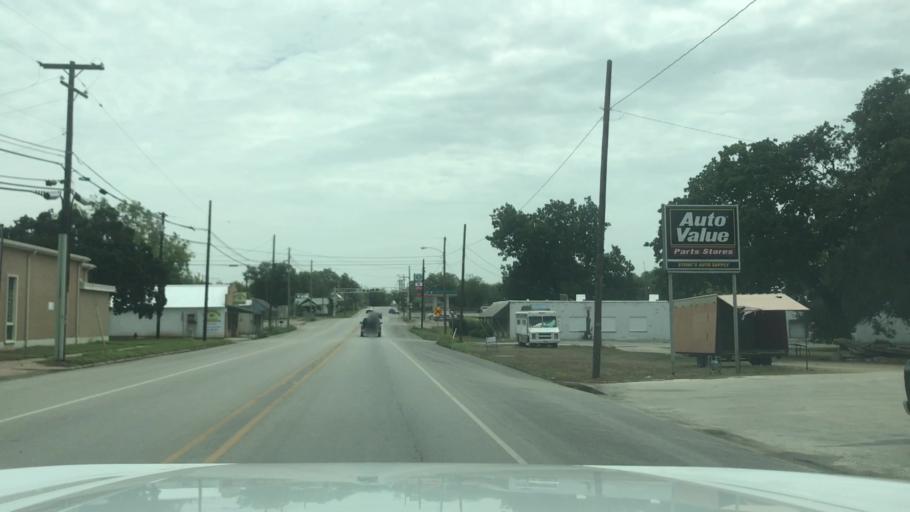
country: US
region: Texas
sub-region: Erath County
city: Dublin
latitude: 32.0847
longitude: -98.3403
